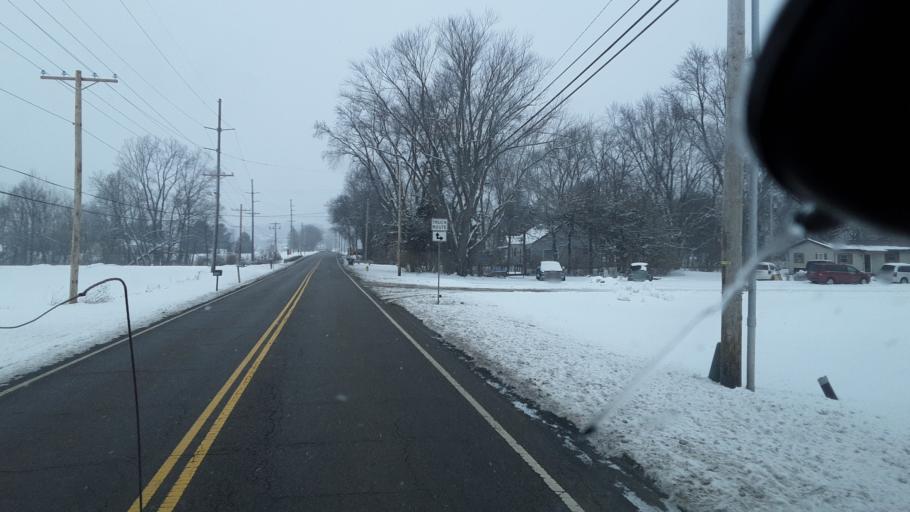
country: US
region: Ohio
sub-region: Licking County
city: Heath
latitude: 40.0247
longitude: -82.4803
